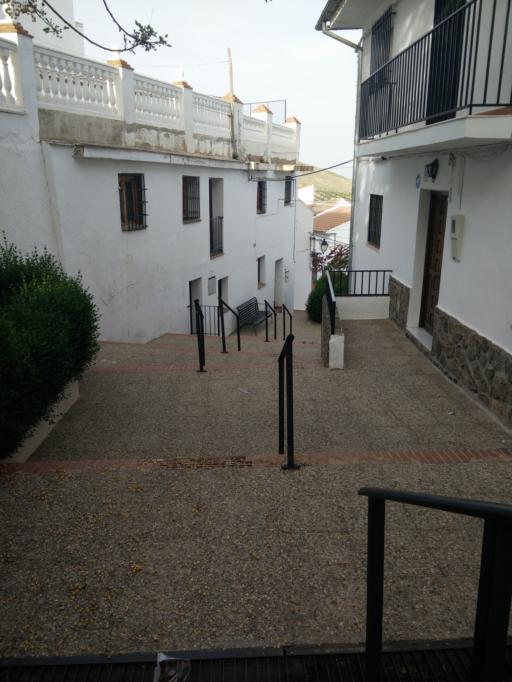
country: ES
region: Andalusia
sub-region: Provincia de Granada
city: Diezma
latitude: 37.3209
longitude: -3.3316
